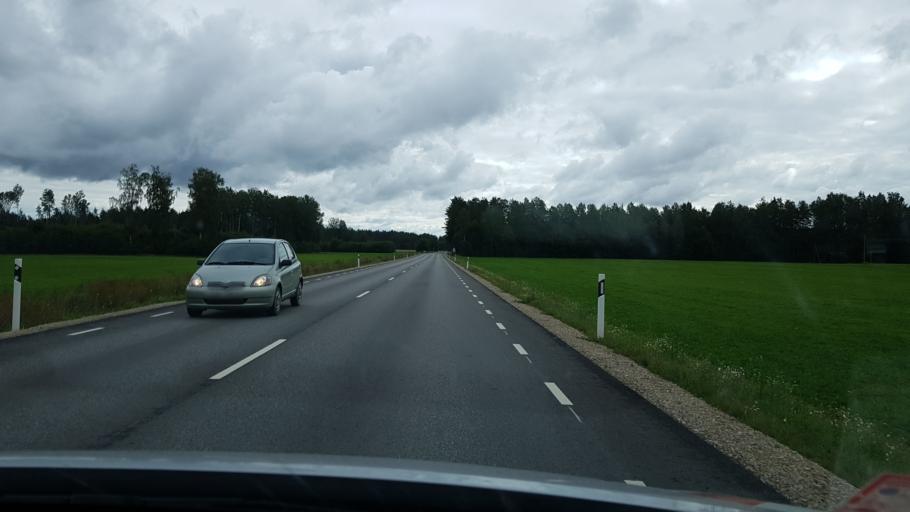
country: EE
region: Polvamaa
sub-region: Polva linn
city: Polva
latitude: 58.0424
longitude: 27.0878
